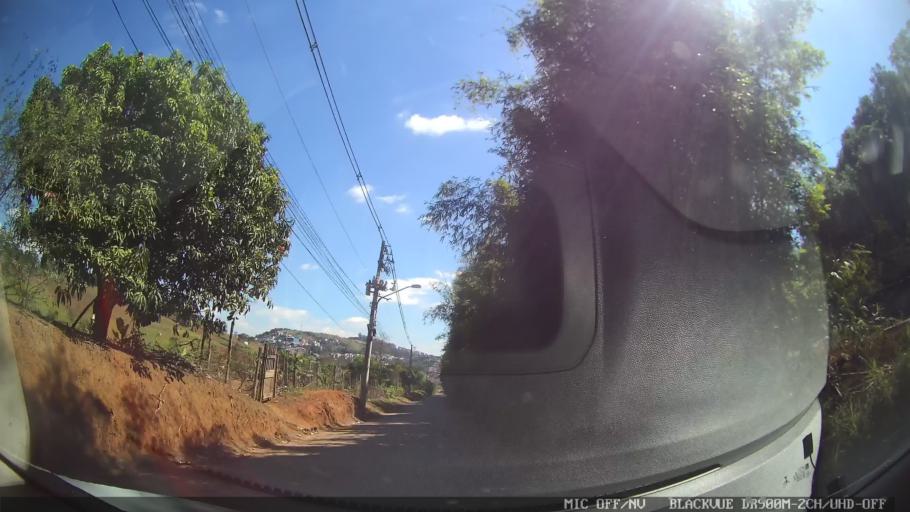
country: BR
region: Sao Paulo
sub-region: Cajamar
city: Cajamar
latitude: -23.4141
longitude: -46.8143
